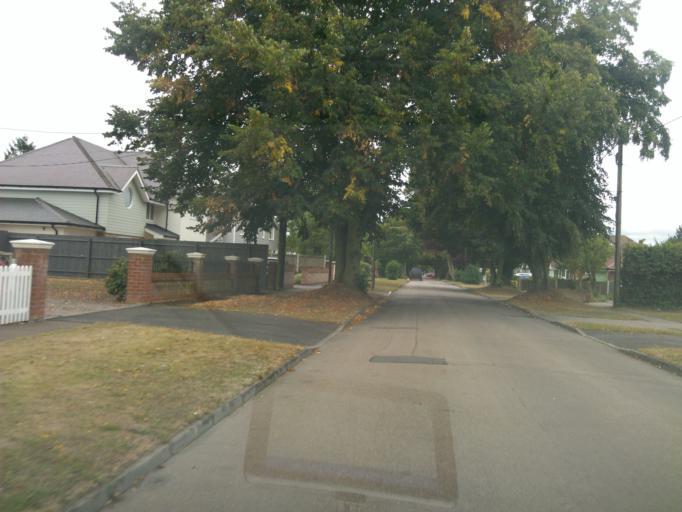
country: GB
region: England
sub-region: Essex
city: West Mersea
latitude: 51.7814
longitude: 0.9282
